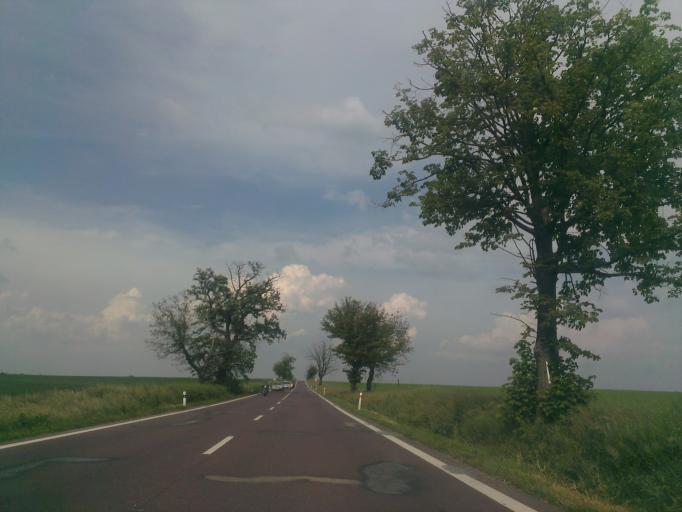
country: CZ
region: South Moravian
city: Miroslav
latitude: 48.9229
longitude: 16.3420
